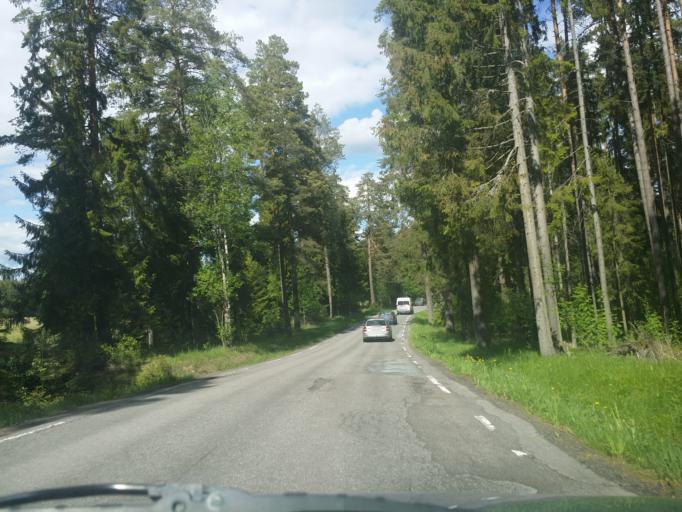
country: NO
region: Oppland
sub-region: Jevnaker
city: Jevnaker
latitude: 60.2319
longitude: 10.3973
